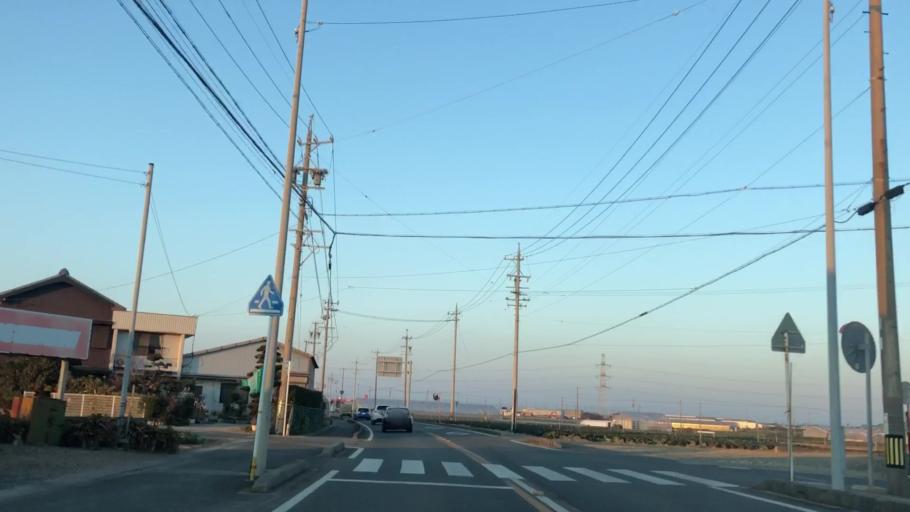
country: JP
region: Aichi
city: Toyohama
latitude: 34.6103
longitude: 137.0725
